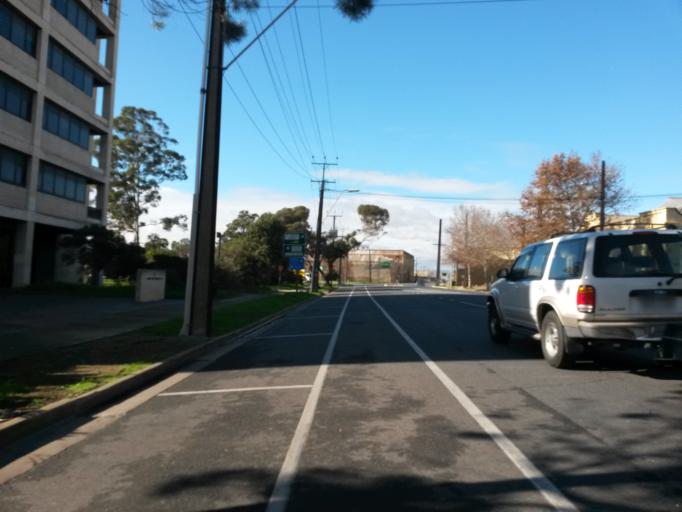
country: AU
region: South Australia
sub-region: Port Adelaide Enfield
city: Birkenhead
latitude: -34.8436
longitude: 138.5091
